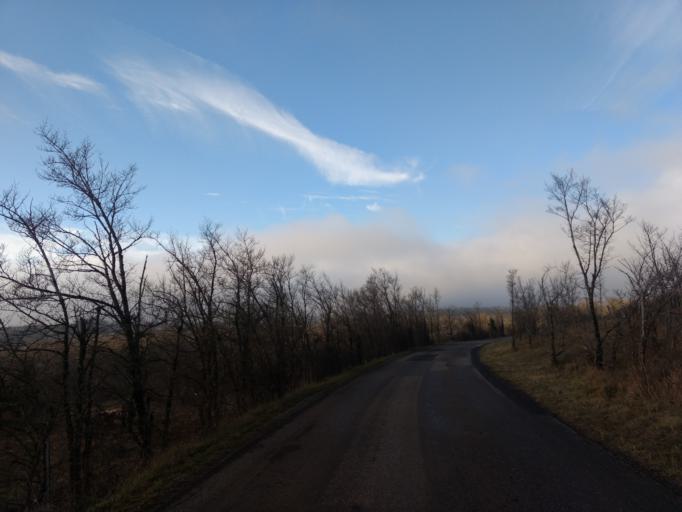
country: FR
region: Midi-Pyrenees
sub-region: Departement de l'Aveyron
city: Salles-la-Source
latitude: 44.4422
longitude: 2.5230
